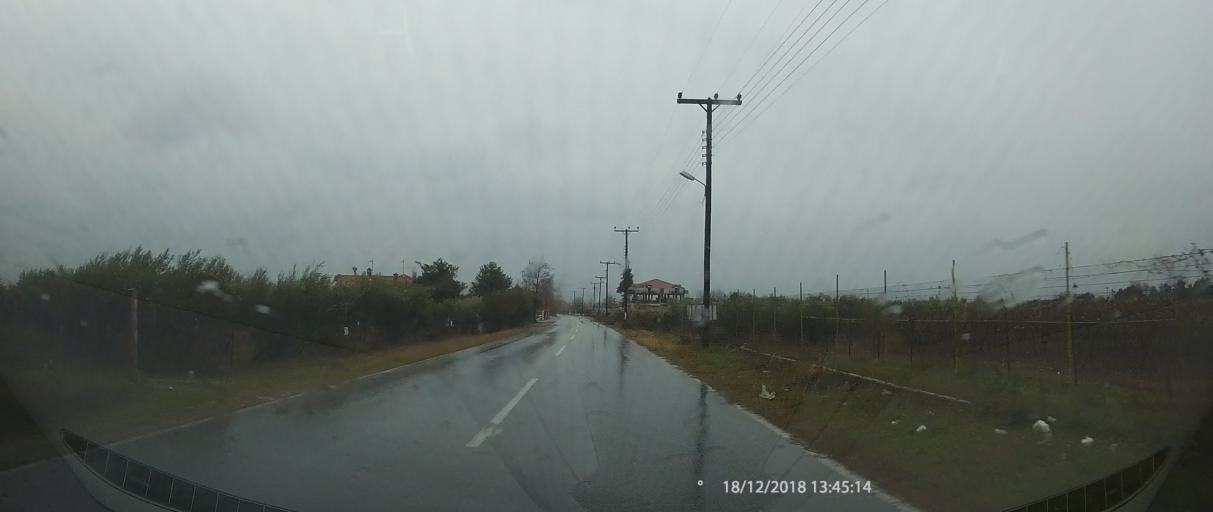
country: GR
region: Central Macedonia
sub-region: Nomos Pierias
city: Leptokarya
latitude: 40.0986
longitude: 22.5419
